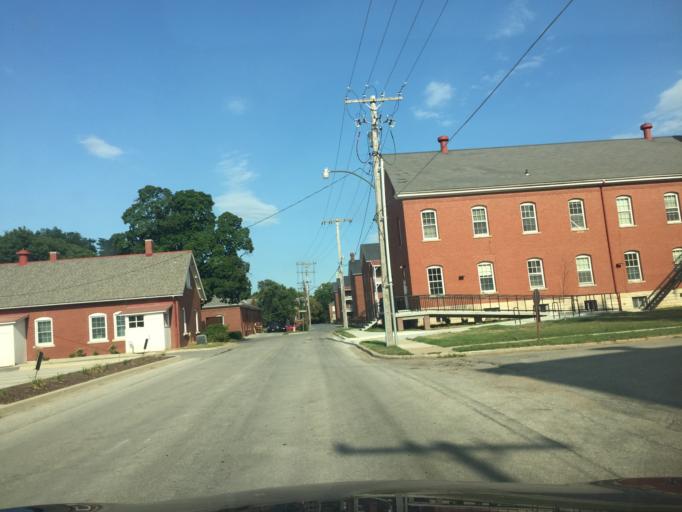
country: US
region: Kansas
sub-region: Leavenworth County
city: Leavenworth
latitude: 39.3564
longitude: -94.9229
